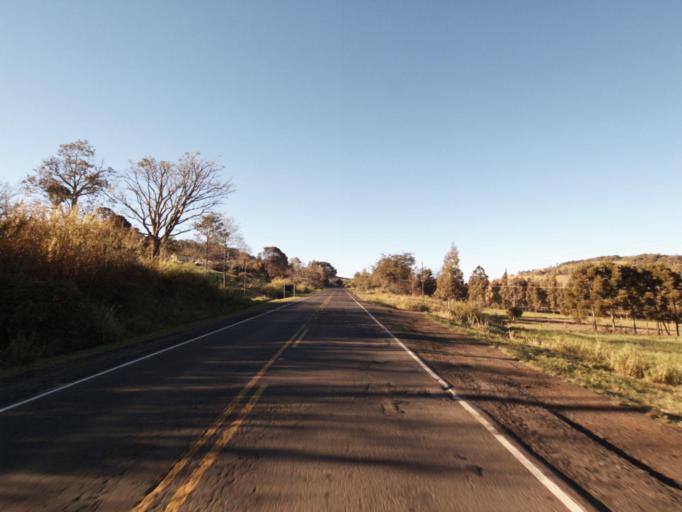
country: AR
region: Misiones
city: Bernardo de Irigoyen
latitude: -26.3714
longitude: -53.5318
